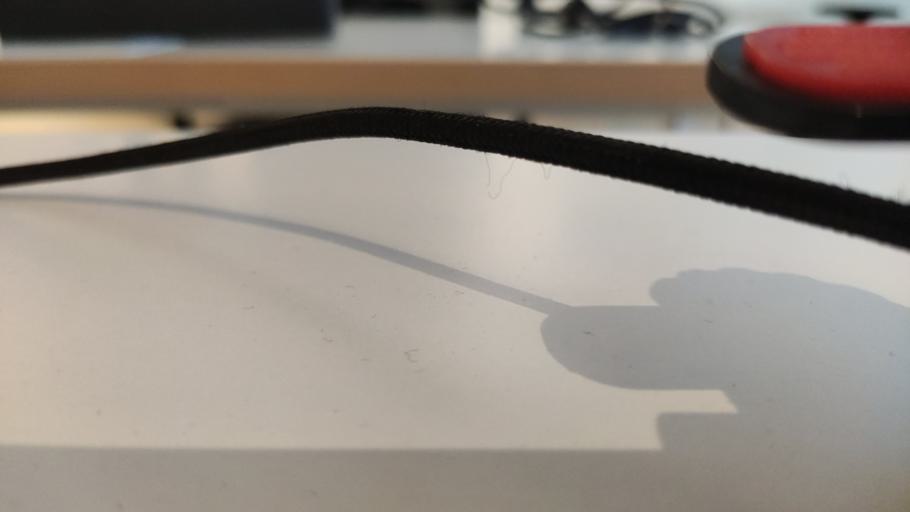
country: RU
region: Moskovskaya
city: Novopetrovskoye
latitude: 55.8784
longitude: 36.4107
